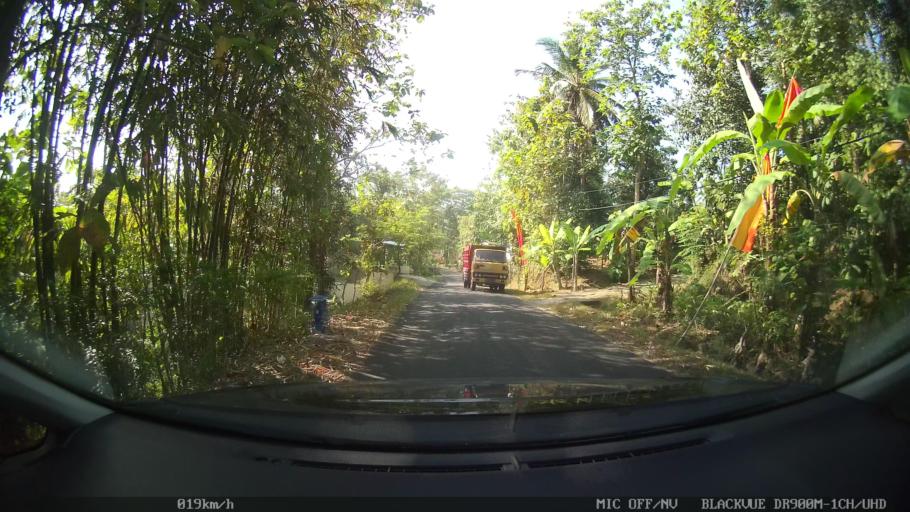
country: ID
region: Daerah Istimewa Yogyakarta
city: Kasihan
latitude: -7.8335
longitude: 110.2753
